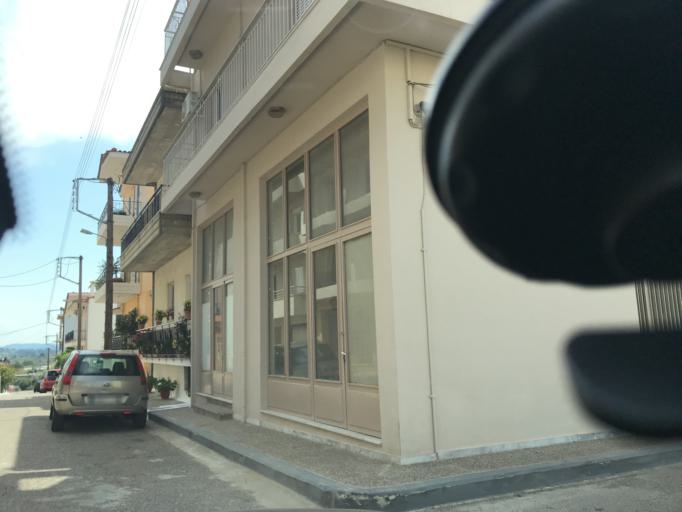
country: GR
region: West Greece
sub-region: Nomos Ileias
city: Pyrgos
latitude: 37.6725
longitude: 21.4481
